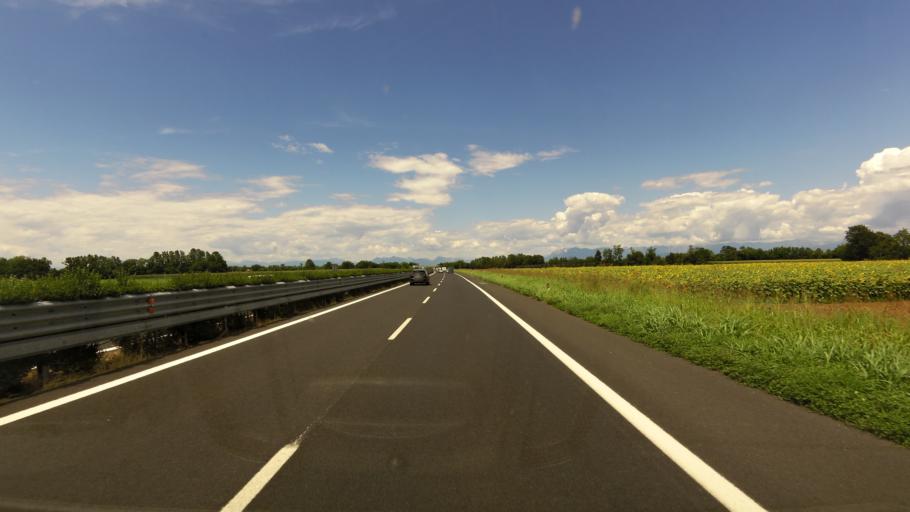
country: IT
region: Friuli Venezia Giulia
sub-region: Provincia di Udine
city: Lauzacco
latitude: 45.9809
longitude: 13.2434
